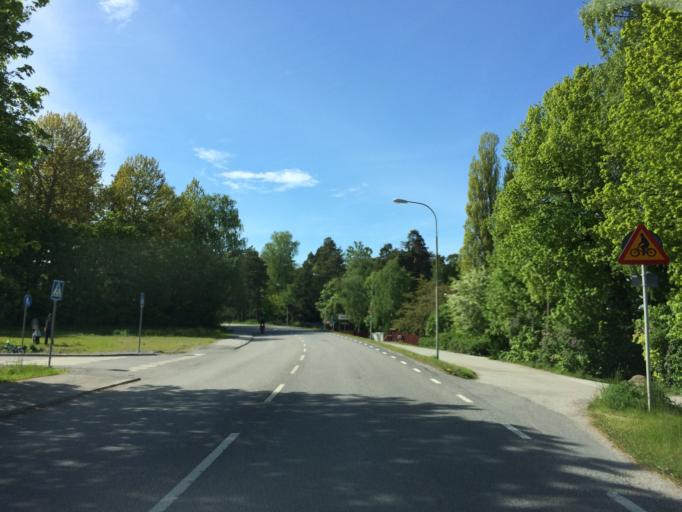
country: SE
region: Stockholm
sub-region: Sollentuna Kommun
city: Sollentuna
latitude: 59.4495
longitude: 17.9371
